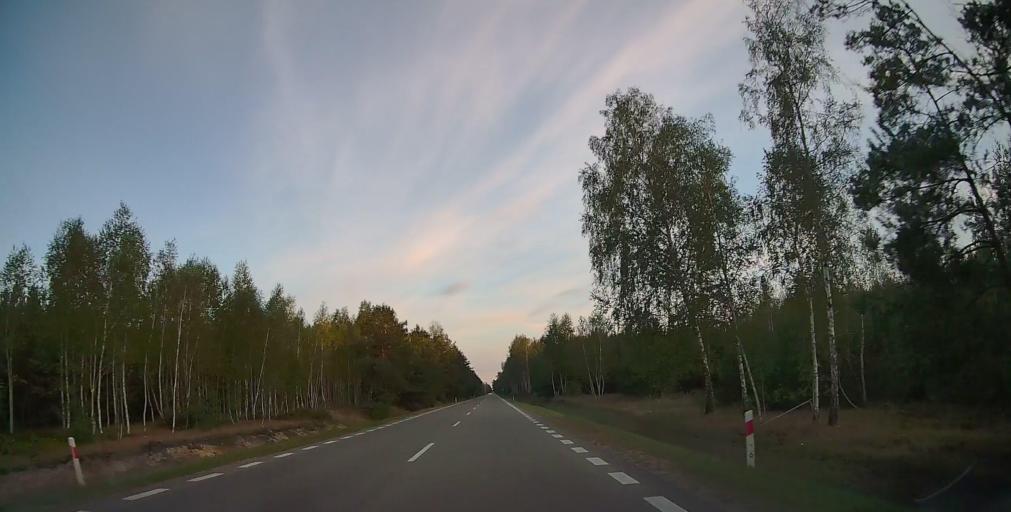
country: PL
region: Masovian Voivodeship
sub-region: Powiat kozienicki
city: Ryczywol
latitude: 51.6428
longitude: 21.4637
